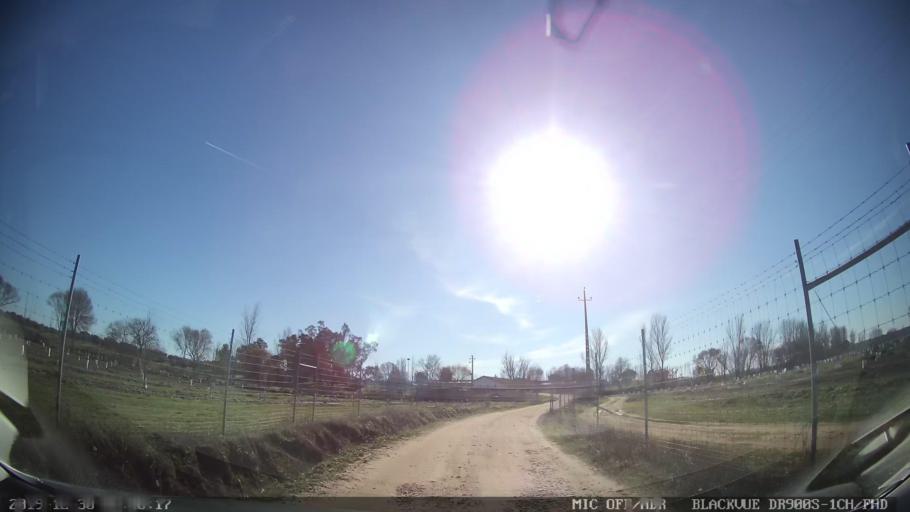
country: PT
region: Castelo Branco
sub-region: Idanha-A-Nova
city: Idanha-a-Nova
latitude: 39.8646
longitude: -7.1351
